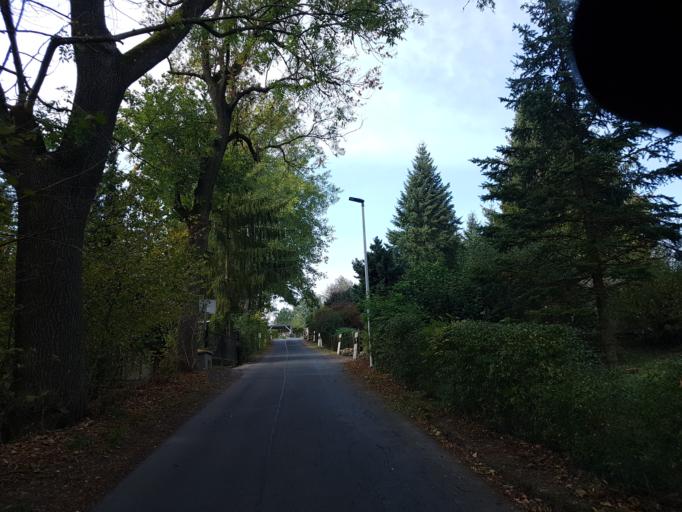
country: DE
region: Saxony
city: Waldheim
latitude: 51.0848
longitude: 13.0054
